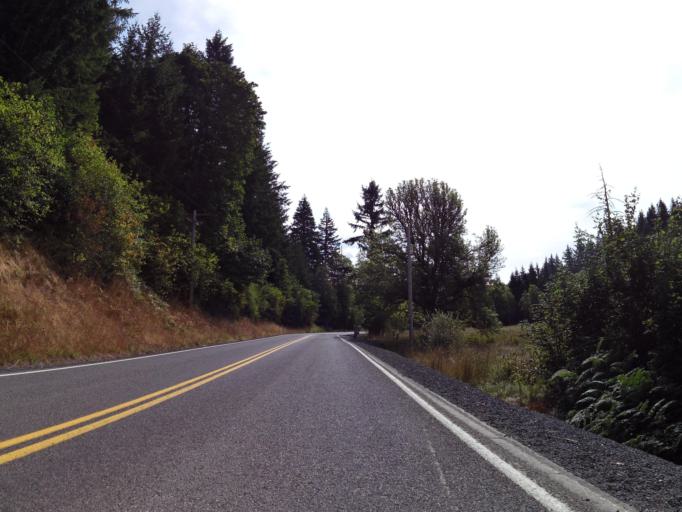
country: US
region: Washington
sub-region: Lewis County
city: Napavine
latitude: 46.5676
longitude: -122.9669
